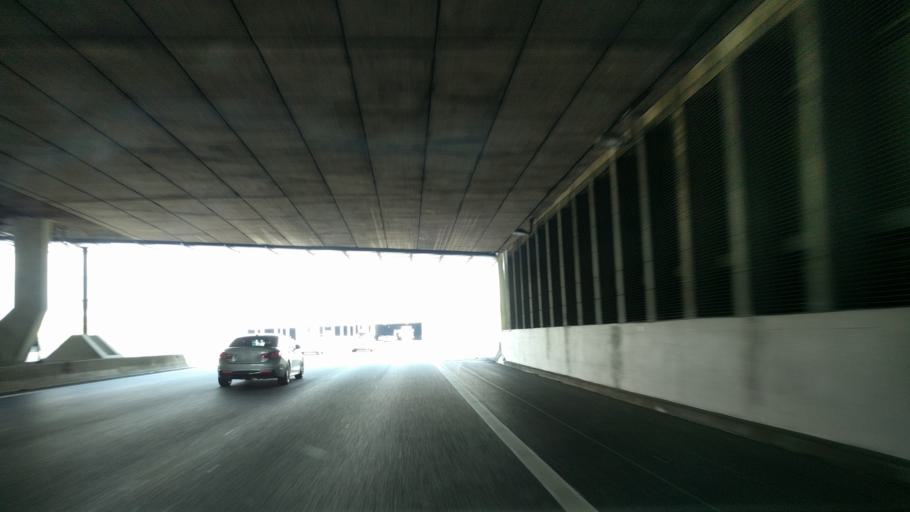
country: FR
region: Ile-de-France
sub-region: Departement du Val-d'Oise
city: Roissy-en-France
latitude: 49.0185
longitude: 2.5331
